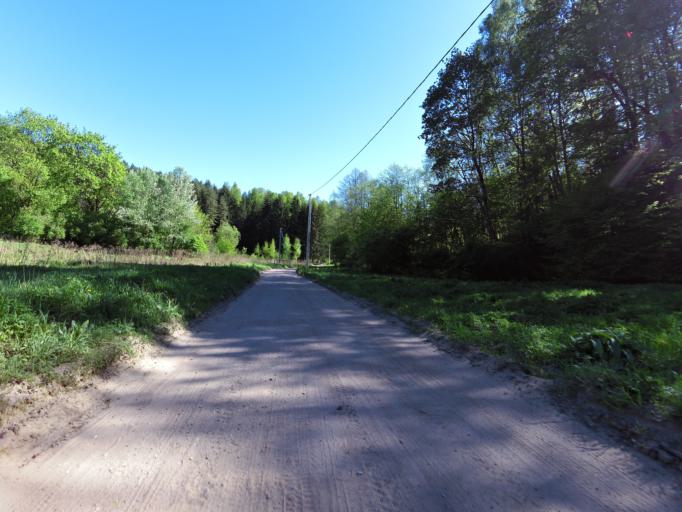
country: LT
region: Vilnius County
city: Pilaite
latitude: 54.6892
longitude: 25.1553
